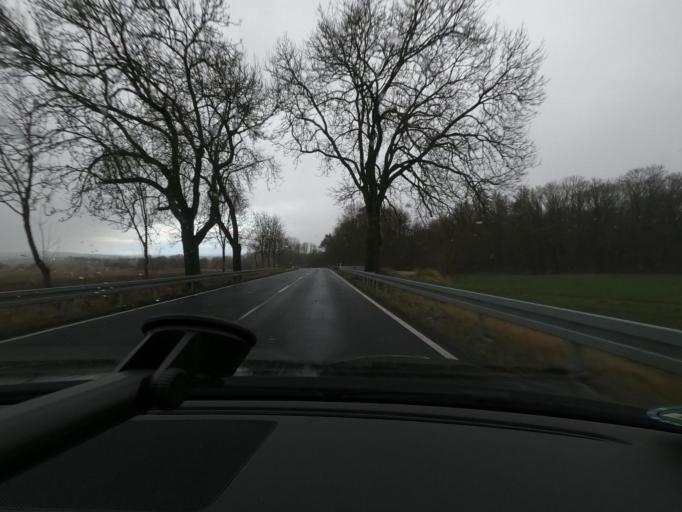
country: DE
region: Thuringia
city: Helmsdorf
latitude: 51.2739
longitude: 10.3674
